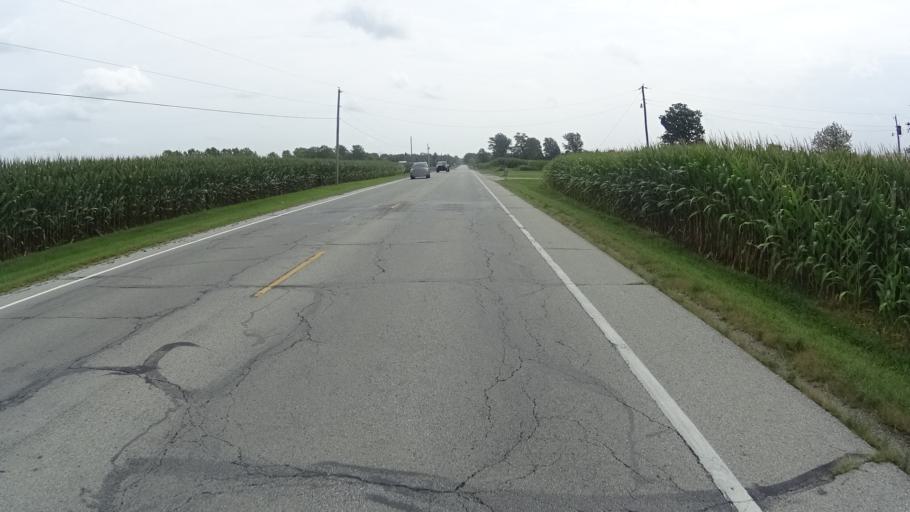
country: US
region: Indiana
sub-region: Madison County
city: Edgewood
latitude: 40.1019
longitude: -85.7801
